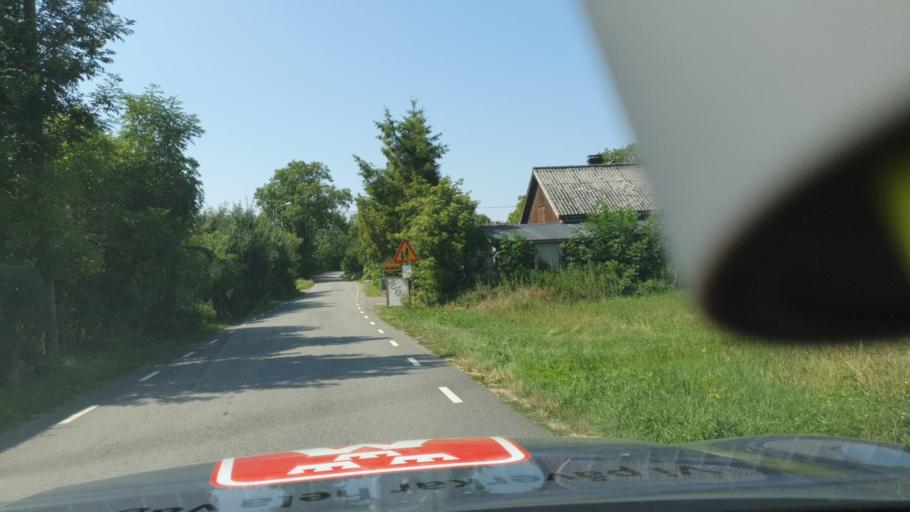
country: SE
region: Skane
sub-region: Kristianstads Kommun
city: Fjalkinge
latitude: 56.0709
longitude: 14.3590
